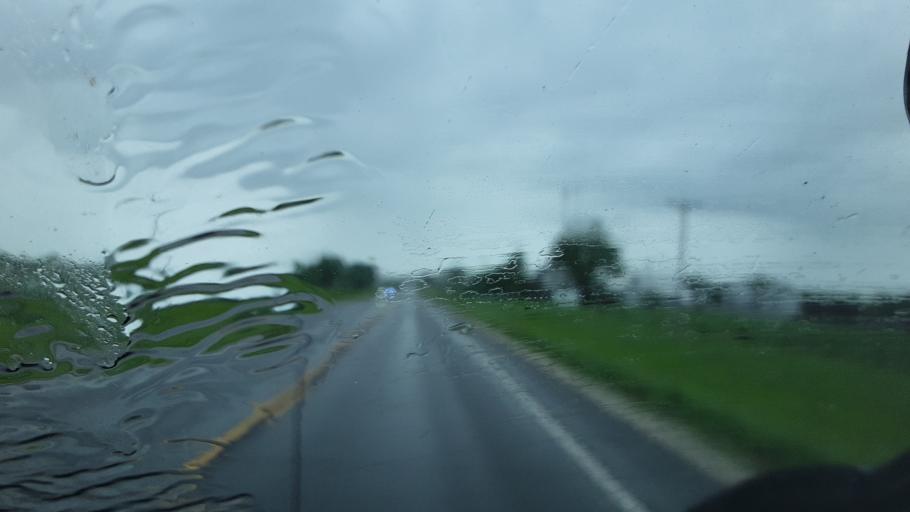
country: US
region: Missouri
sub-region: Monroe County
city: Paris
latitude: 39.4804
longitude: -92.1634
